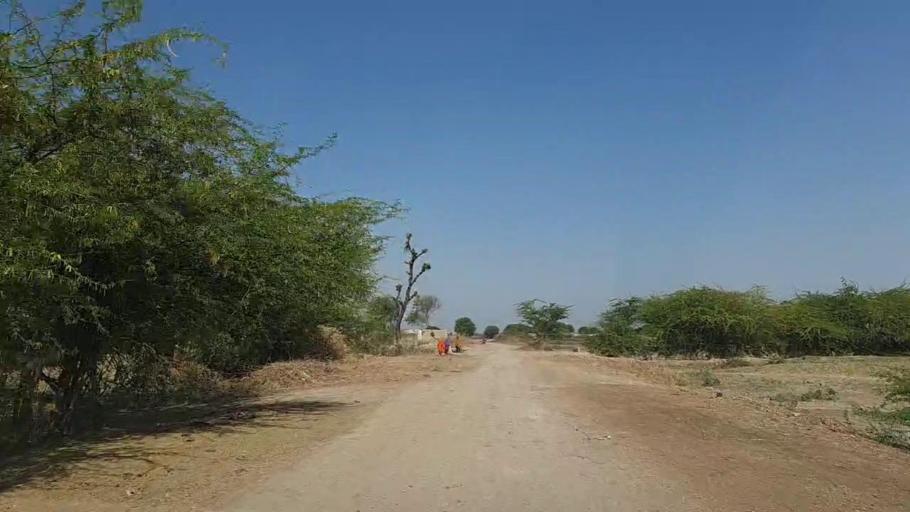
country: PK
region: Sindh
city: Samaro
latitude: 25.2474
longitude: 69.4484
